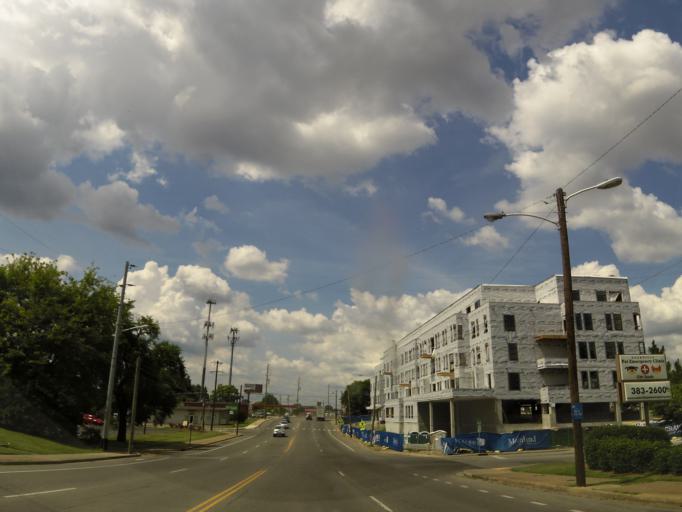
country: US
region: Tennessee
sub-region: Davidson County
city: Nashville
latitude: 36.1334
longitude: -86.7888
